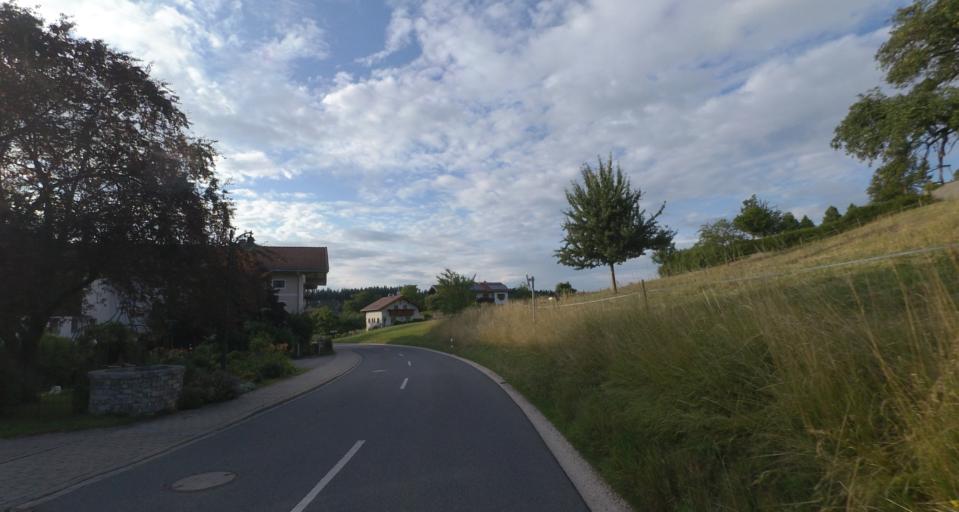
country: DE
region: Bavaria
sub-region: Upper Bavaria
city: Nussdorf
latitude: 47.9066
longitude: 12.5945
